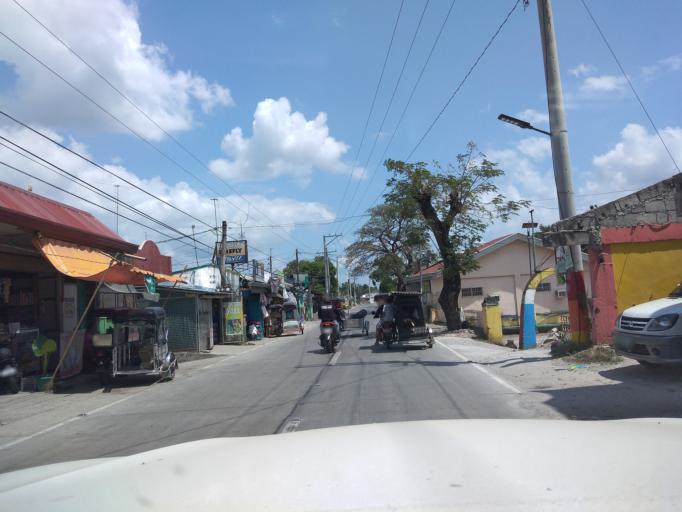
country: PH
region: Central Luzon
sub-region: Province of Pampanga
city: Lourdes
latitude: 15.0194
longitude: 120.8610
